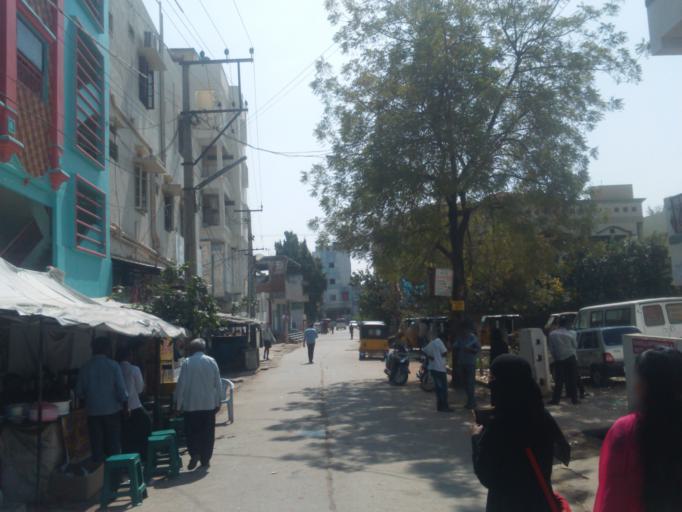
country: IN
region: Telangana
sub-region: Mahbubnagar
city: Alampur
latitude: 15.8239
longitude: 78.0411
